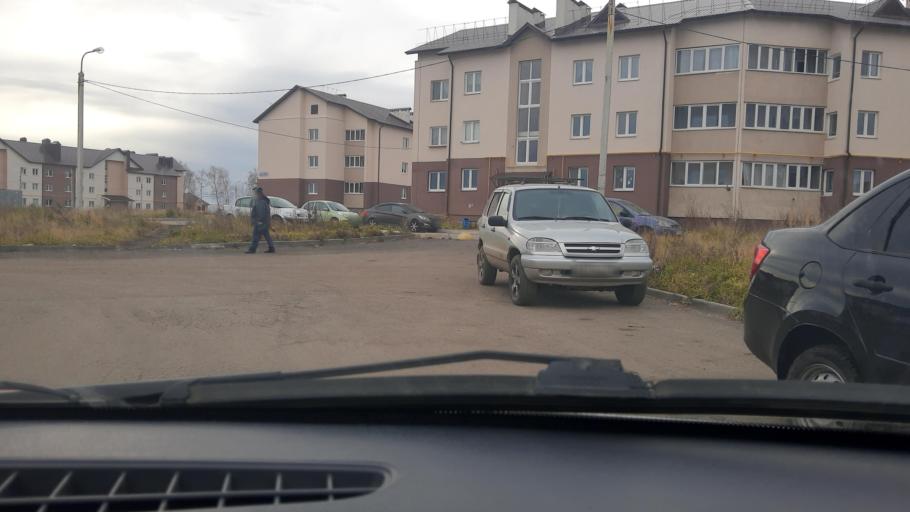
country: RU
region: Bashkortostan
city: Avdon
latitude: 54.6966
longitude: 55.8048
